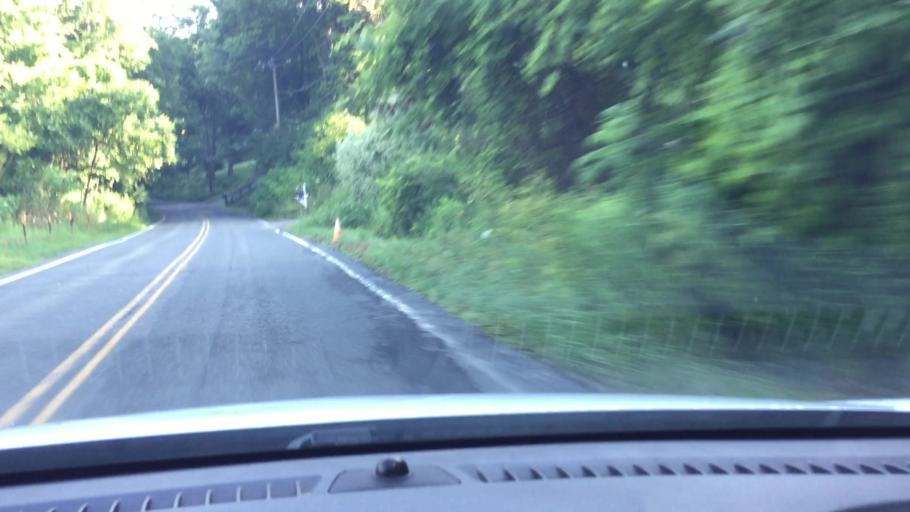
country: US
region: Massachusetts
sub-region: Berkshire County
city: Pittsfield
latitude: 42.4055
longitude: -73.2318
